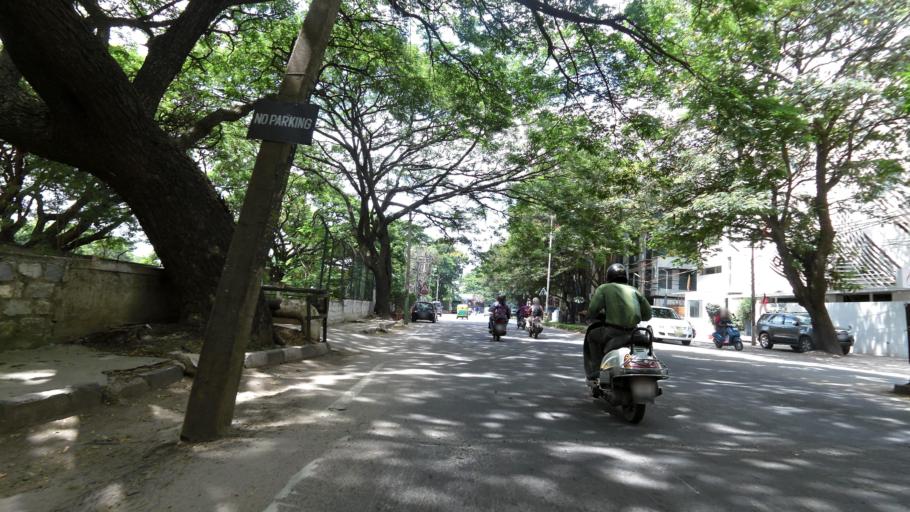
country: IN
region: Karnataka
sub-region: Bangalore Urban
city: Bangalore
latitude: 12.9898
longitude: 77.6196
